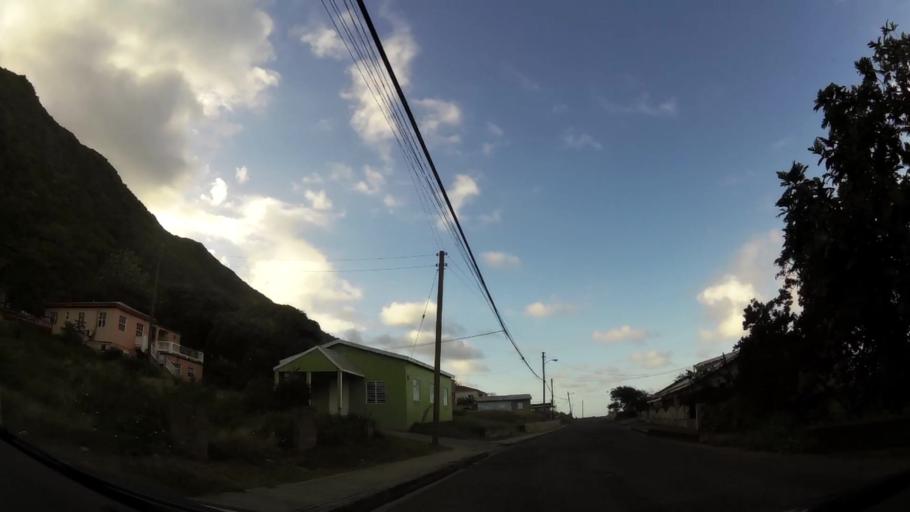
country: KN
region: Saint Mary Cayon
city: Cayon
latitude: 17.3413
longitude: -62.7134
